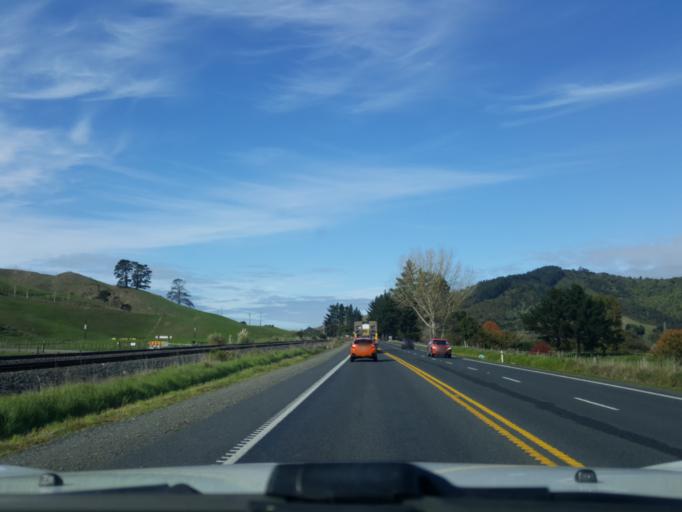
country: NZ
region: Waikato
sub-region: Waikato District
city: Ngaruawahia
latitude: -37.5952
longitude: 175.1612
